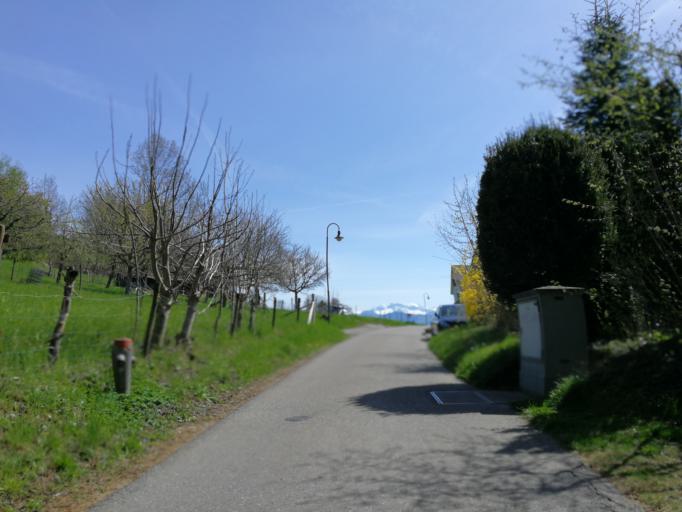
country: CH
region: Zurich
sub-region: Bezirk Meilen
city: Feldmeilen
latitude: 47.2771
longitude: 8.6288
